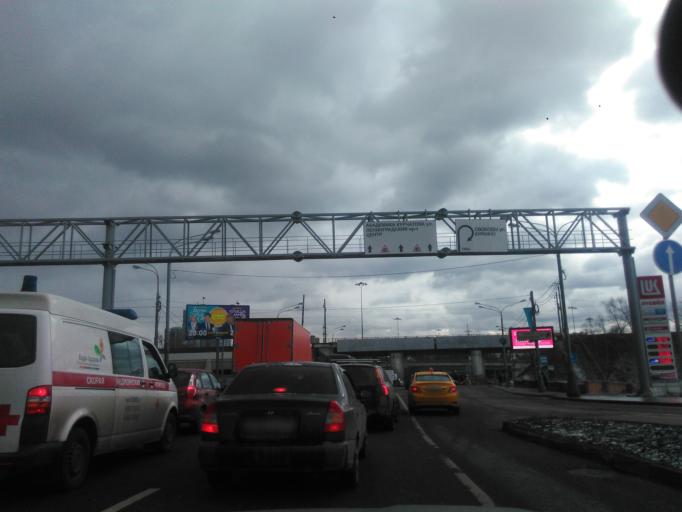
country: RU
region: Moscow
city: Pokrovskoye-Streshnevo
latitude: 55.8212
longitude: 37.4460
